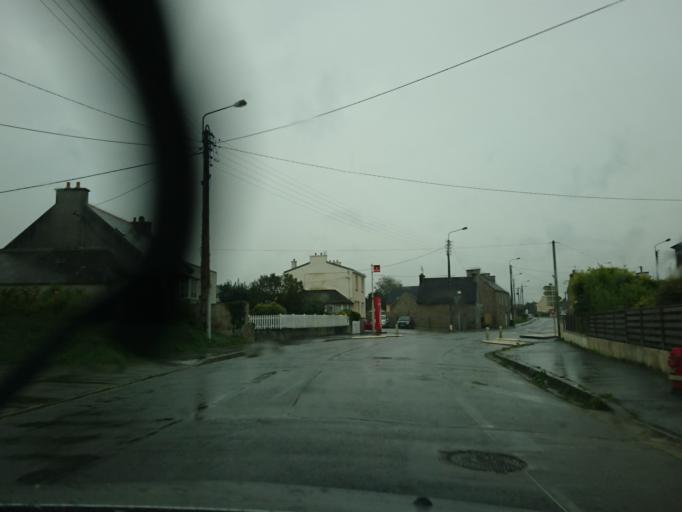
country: FR
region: Brittany
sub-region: Departement du Finistere
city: Plouvien
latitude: 48.5284
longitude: -4.4521
